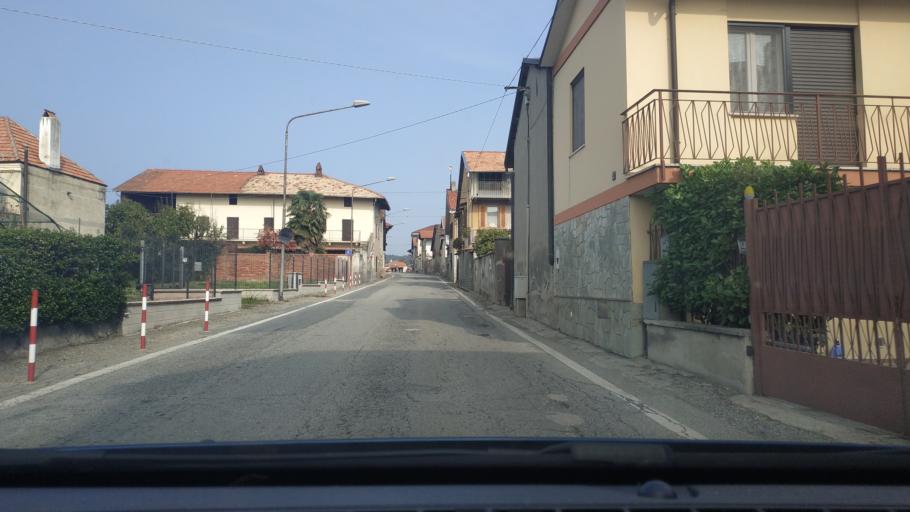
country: IT
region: Piedmont
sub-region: Provincia di Torino
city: Montalenghe
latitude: 45.3348
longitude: 7.8355
